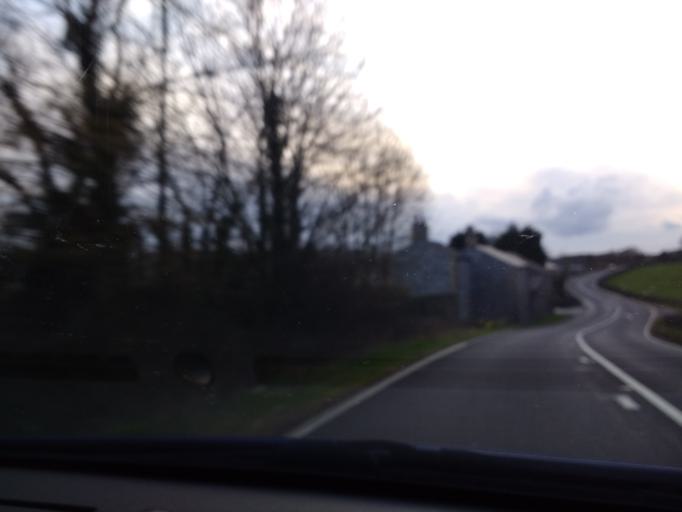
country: GB
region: England
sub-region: North Yorkshire
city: Settle
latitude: 54.1035
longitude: -2.3576
